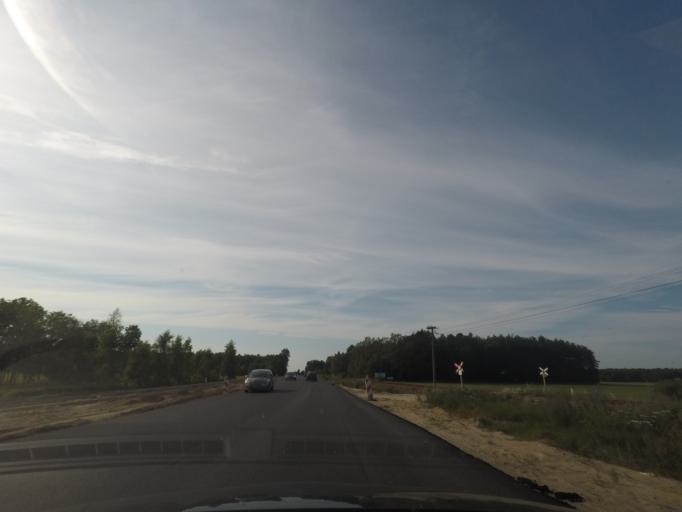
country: PL
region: Pomeranian Voivodeship
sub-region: Powiat leborski
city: Leba
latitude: 54.7295
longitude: 17.5670
